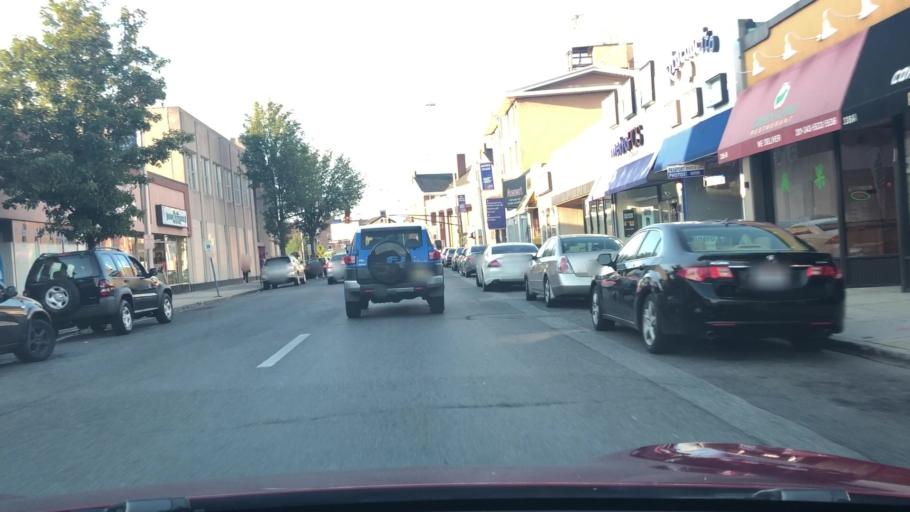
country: US
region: New Jersey
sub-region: Bergen County
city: Hackensack
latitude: 40.8888
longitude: -74.0403
